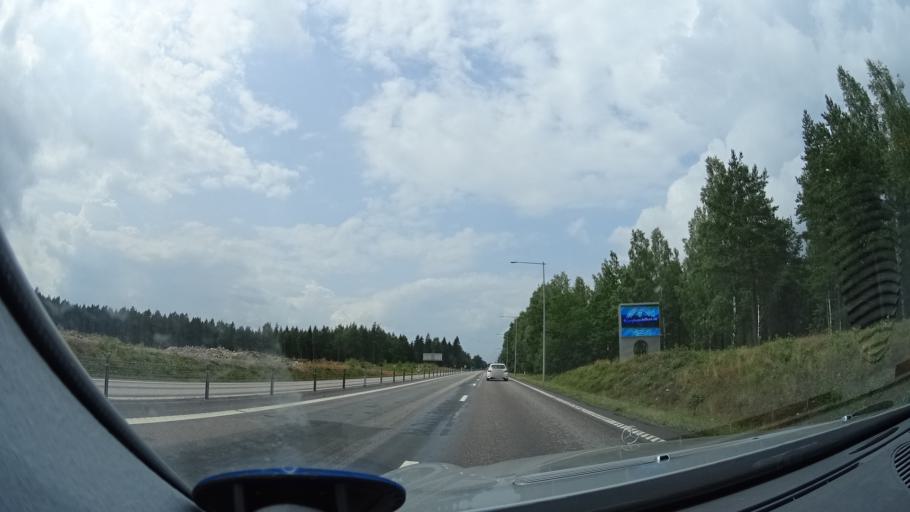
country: SE
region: Kalmar
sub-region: Nybro Kommun
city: Nybro
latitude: 56.7308
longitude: 15.9617
